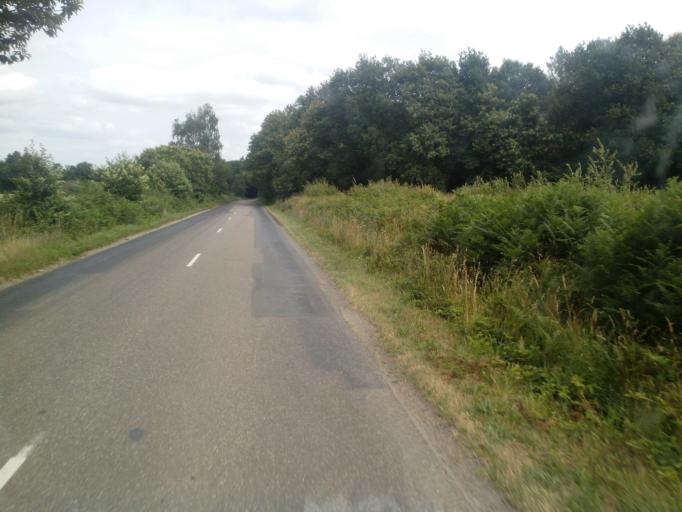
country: FR
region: Brittany
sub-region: Departement d'Ille-et-Vilaine
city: Maxent
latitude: 47.9879
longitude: -2.0557
